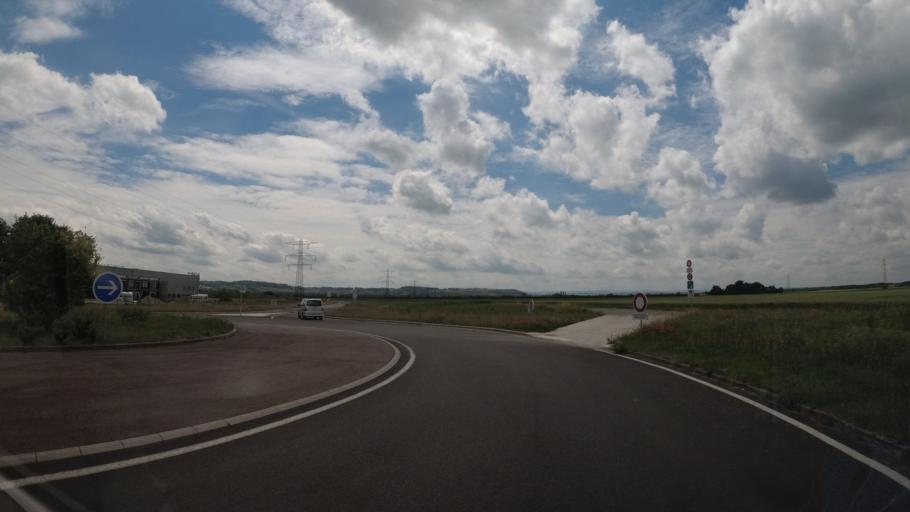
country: FR
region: Alsace
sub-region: Departement du Haut-Rhin
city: Ottmarsheim
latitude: 47.7530
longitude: 7.5202
